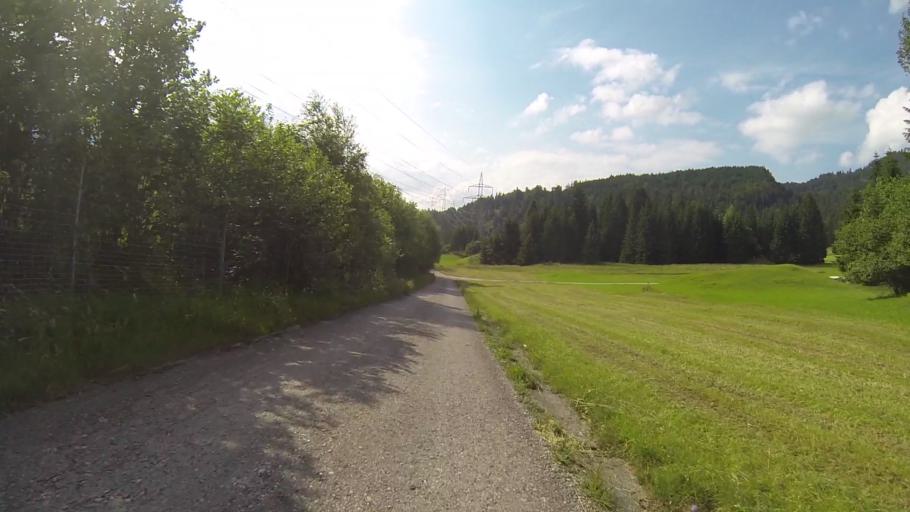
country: AT
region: Tyrol
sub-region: Politischer Bezirk Reutte
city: Pflach
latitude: 47.5185
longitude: 10.7249
